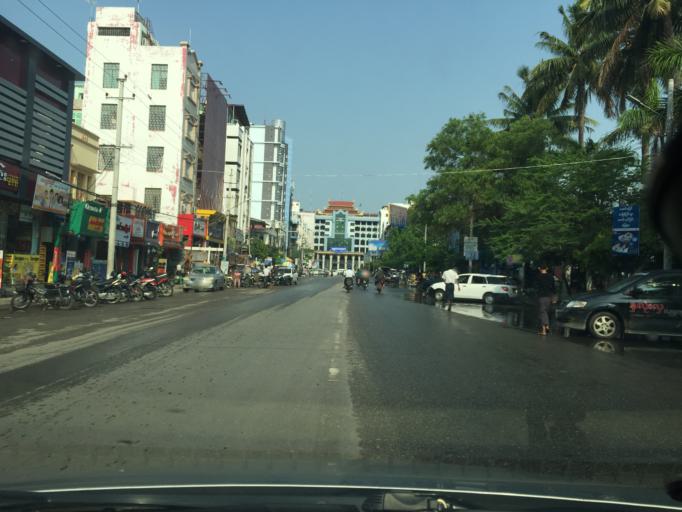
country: MM
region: Mandalay
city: Mandalay
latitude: 21.9767
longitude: 96.0898
